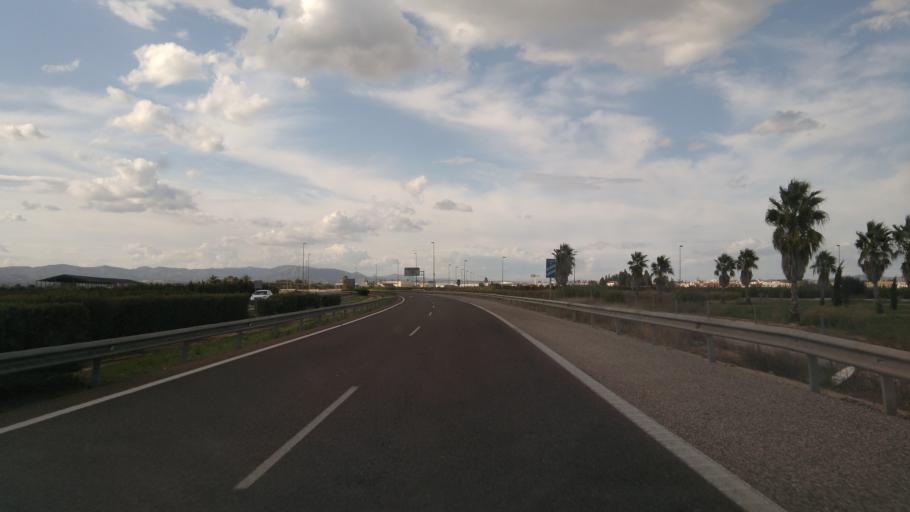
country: ES
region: Valencia
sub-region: Provincia de Valencia
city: Guadassuar
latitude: 39.1747
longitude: -0.4683
